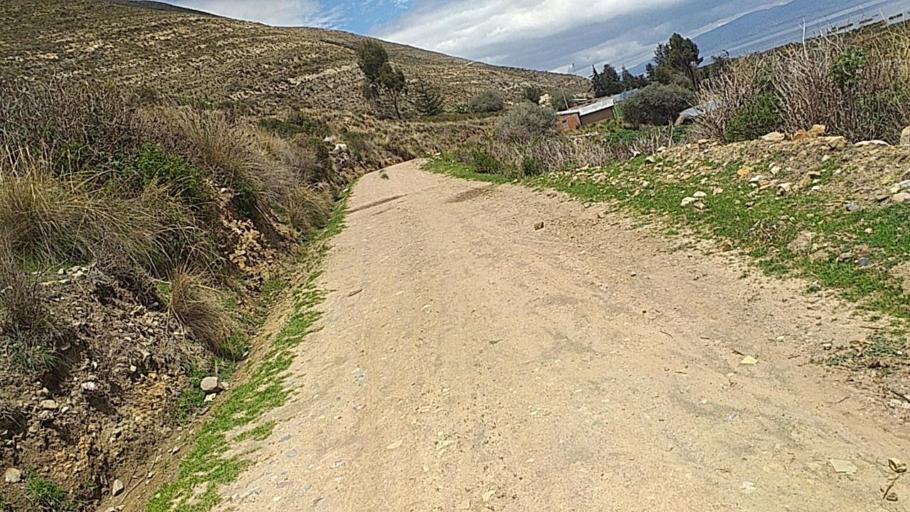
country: BO
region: La Paz
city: Huatajata
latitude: -16.3214
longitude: -68.6677
